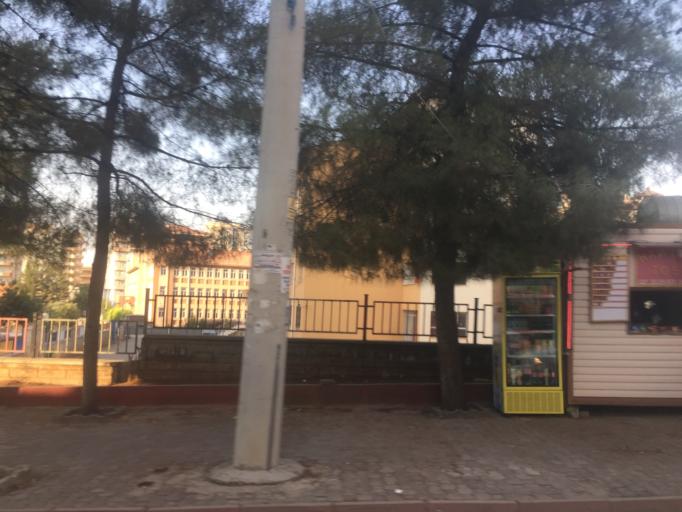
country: TR
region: Mardin
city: Midyat
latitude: 37.4301
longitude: 41.3376
